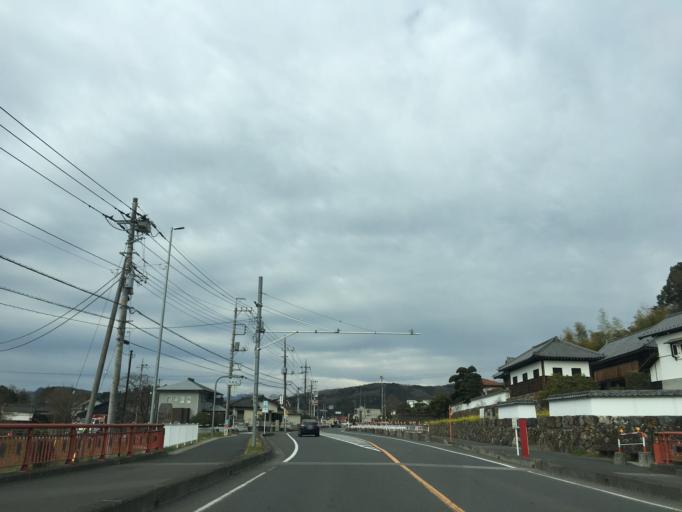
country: JP
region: Saitama
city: Hanno
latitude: 35.8861
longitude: 139.3119
